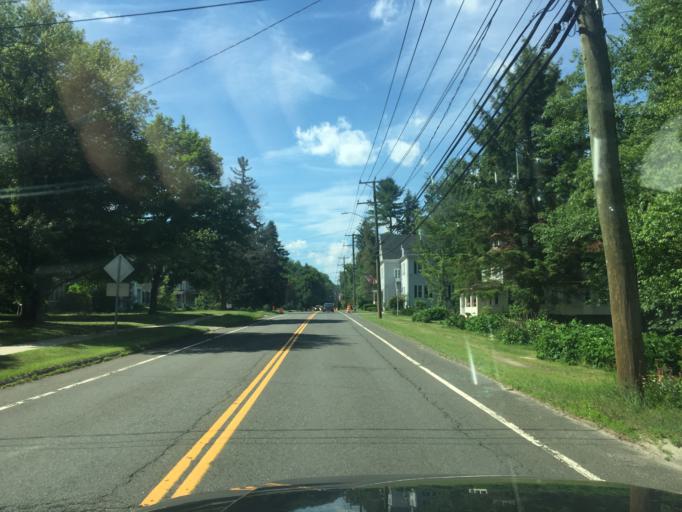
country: US
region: Connecticut
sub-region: Litchfield County
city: New Hartford Center
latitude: 41.8806
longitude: -72.9809
